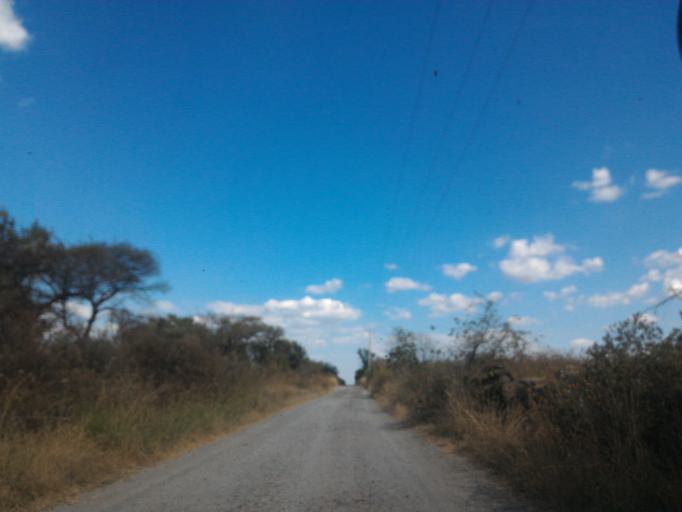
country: MX
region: Jalisco
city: San Diego de Alejandria
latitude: 20.8830
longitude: -102.0050
